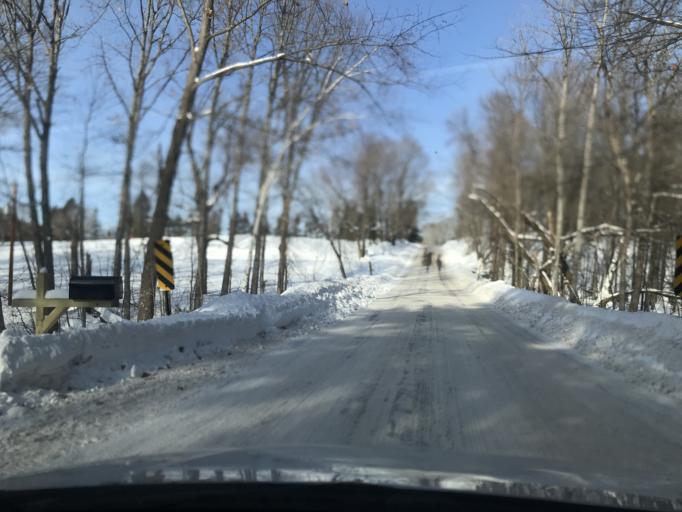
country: US
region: Wisconsin
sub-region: Menominee County
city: Legend Lake
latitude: 45.2991
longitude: -88.4918
